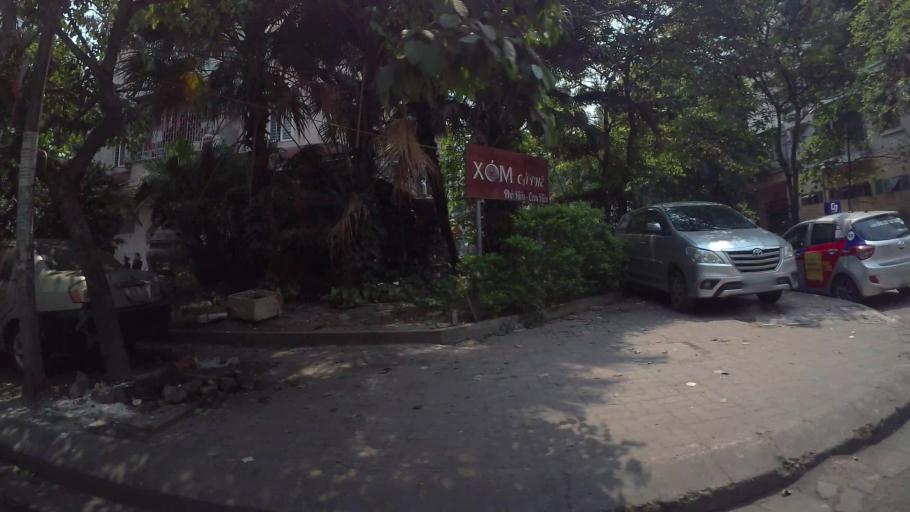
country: VN
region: Ha Noi
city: Thanh Xuan
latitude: 21.0057
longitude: 105.8031
